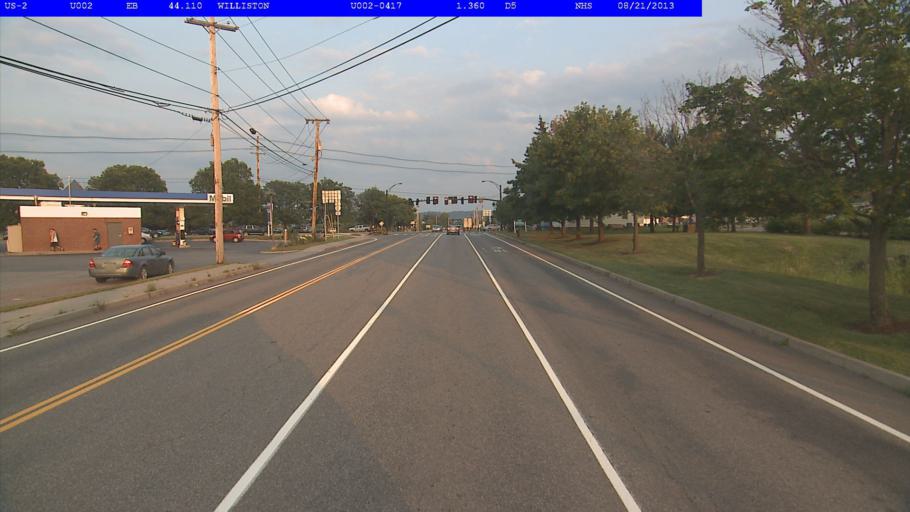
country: US
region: Vermont
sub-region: Chittenden County
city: Essex Junction
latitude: 44.4501
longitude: -73.1122
